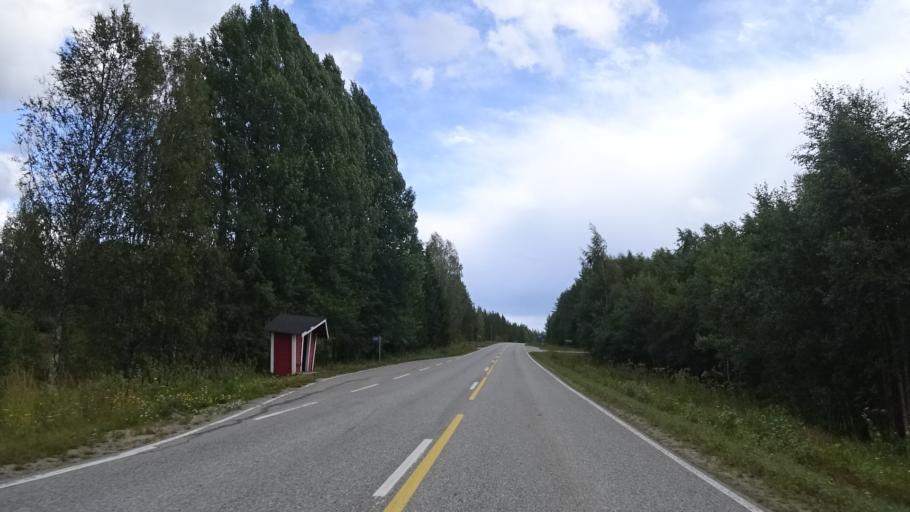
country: FI
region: North Karelia
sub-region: Joensuu
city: Ilomantsi
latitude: 62.6471
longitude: 31.0272
